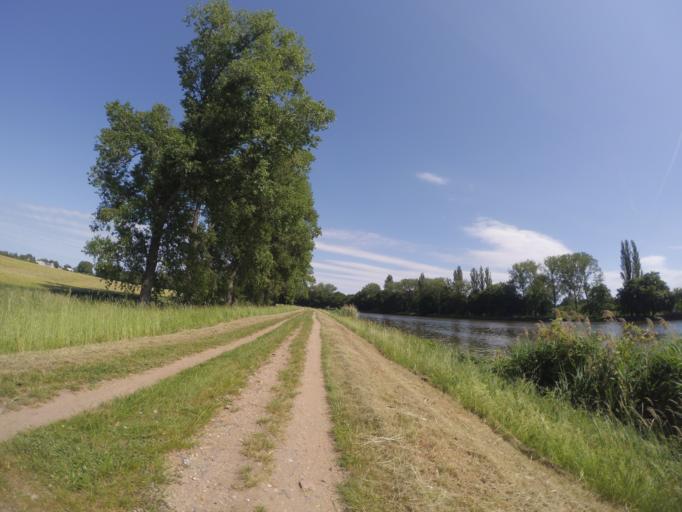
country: CZ
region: Central Bohemia
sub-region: Okres Nymburk
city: Sadska
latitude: 50.1699
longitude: 14.9936
